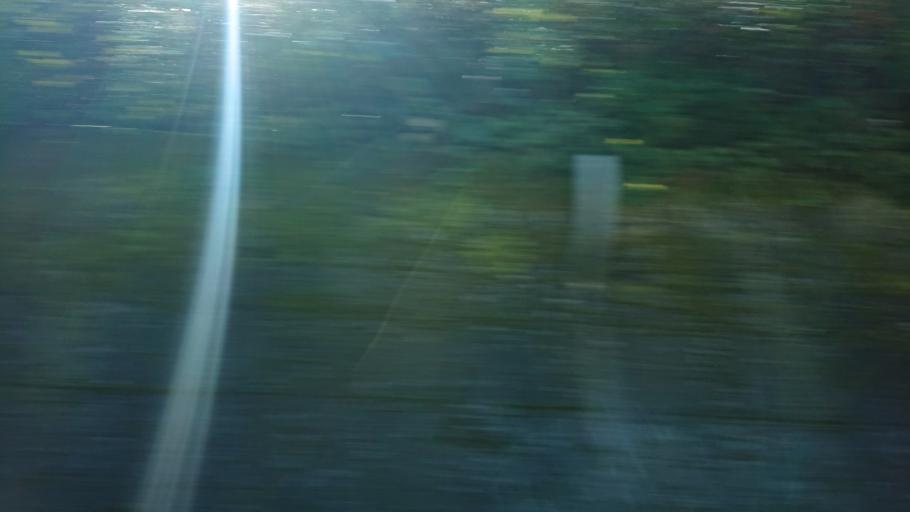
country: TW
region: Taiwan
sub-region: Hualien
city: Hualian
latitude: 24.3628
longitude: 121.3351
